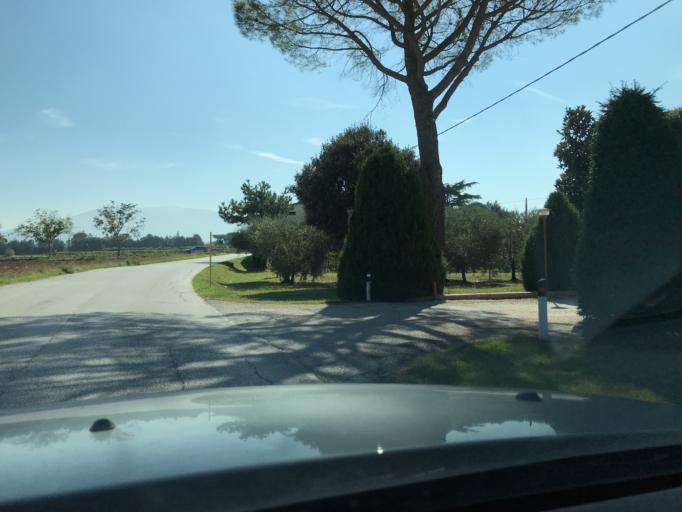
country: IT
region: Umbria
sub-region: Provincia di Perugia
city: Via Lippia
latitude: 43.0959
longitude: 12.4934
